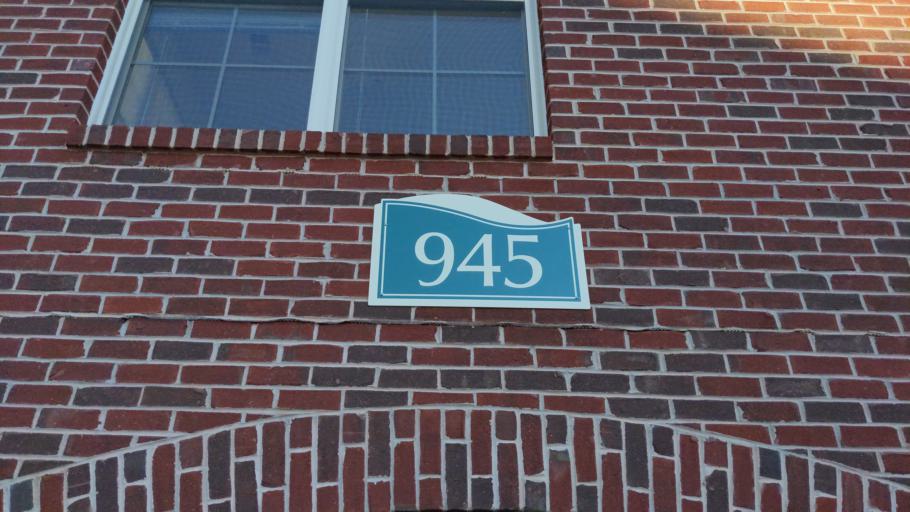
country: US
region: Virginia
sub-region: Montgomery County
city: Merrimac
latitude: 37.1861
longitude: -80.4188
